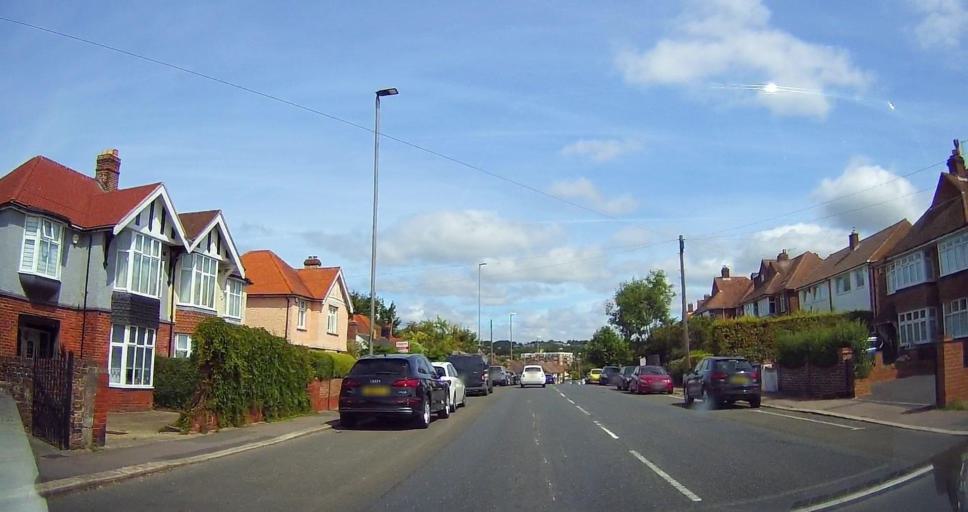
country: GB
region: England
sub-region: East Sussex
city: Saint Leonards-on-Sea
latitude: 50.8722
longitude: 0.5583
